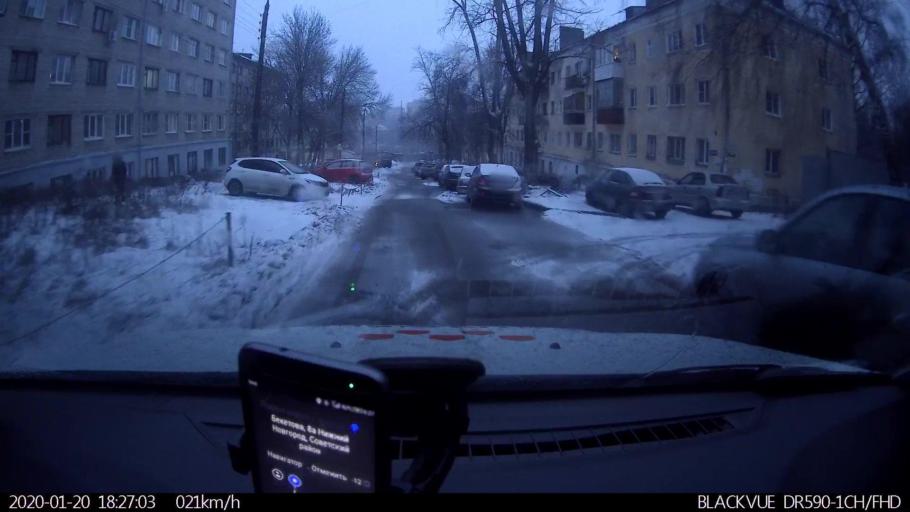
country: RU
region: Nizjnij Novgorod
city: Nizhniy Novgorod
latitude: 56.2915
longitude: 43.9914
